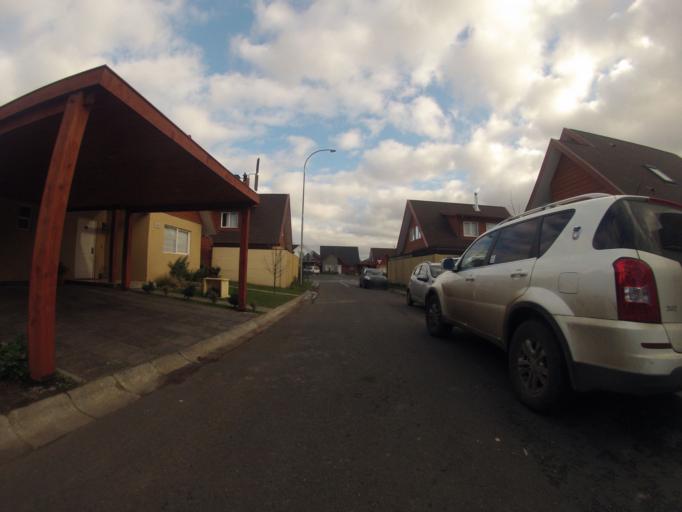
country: CL
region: Araucania
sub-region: Provincia de Cautin
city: Temuco
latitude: -38.7389
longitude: -72.6475
